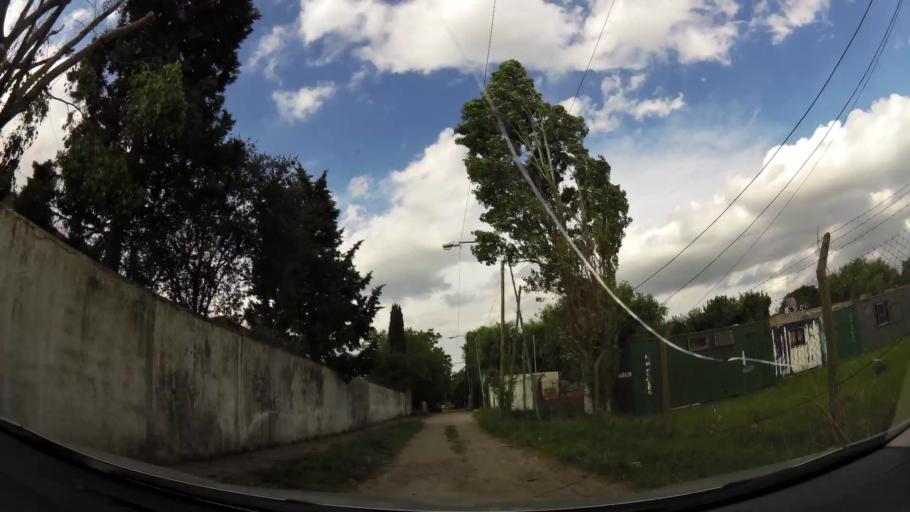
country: AR
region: Buenos Aires
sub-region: Partido de Tigre
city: Tigre
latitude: -34.4759
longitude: -58.6551
